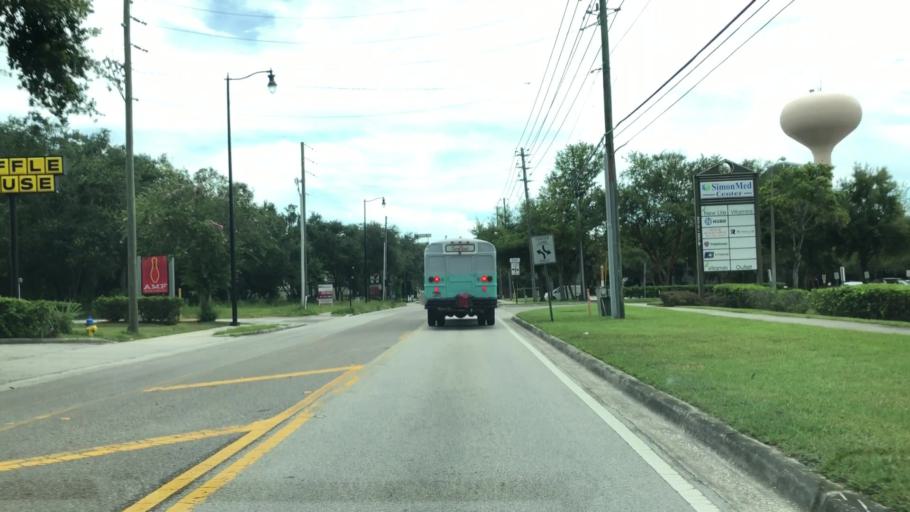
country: US
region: Florida
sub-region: Seminole County
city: Altamonte Springs
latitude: 28.6649
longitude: -81.3903
